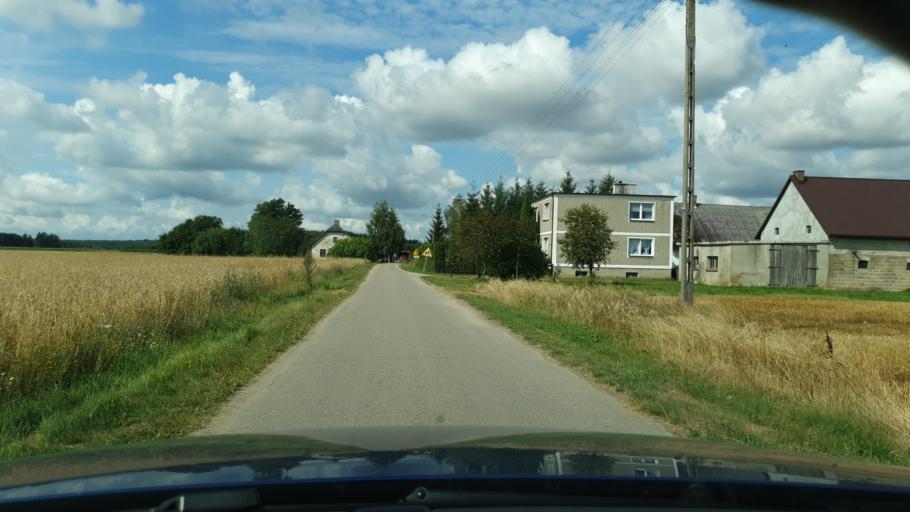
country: PL
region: Pomeranian Voivodeship
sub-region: Powiat czluchowski
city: Przechlewo
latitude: 53.8074
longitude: 17.3752
